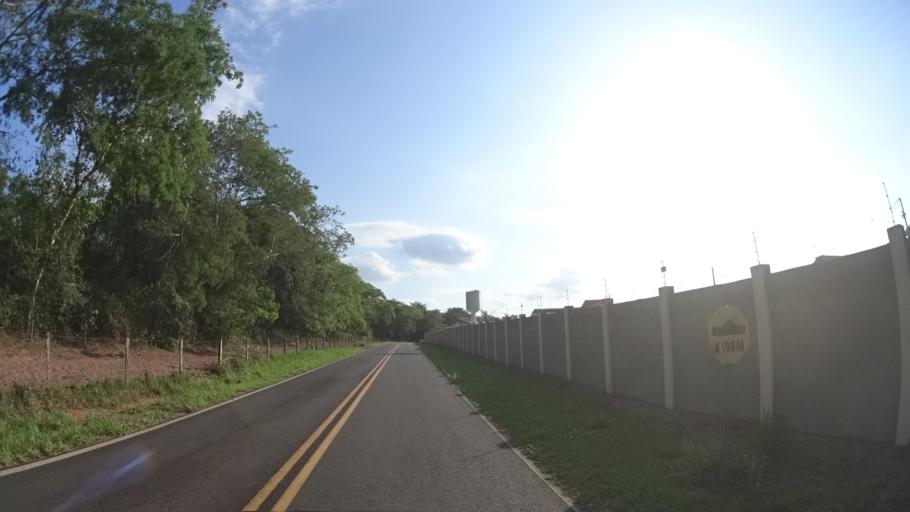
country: BR
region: Sao Paulo
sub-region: Novo Horizonte
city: Novo Horizonte
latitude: -21.4043
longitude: -49.5183
